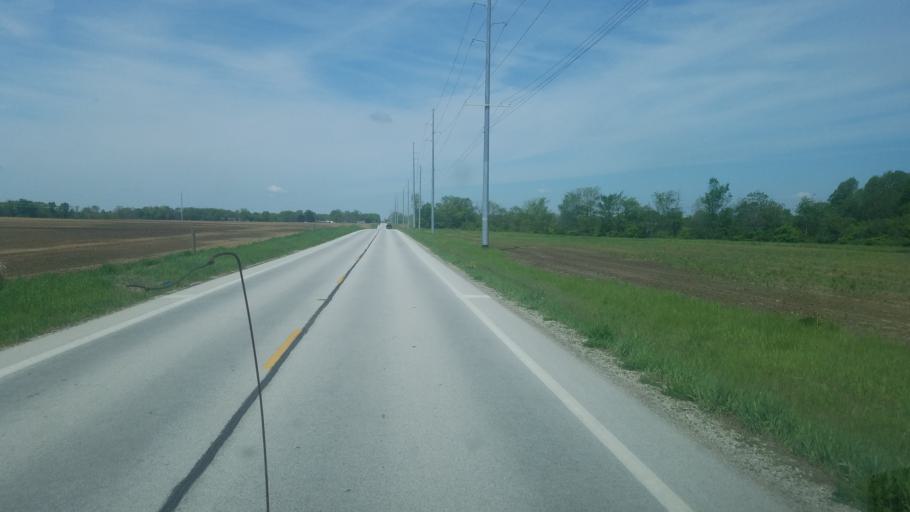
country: US
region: Ohio
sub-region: Seneca County
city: Tiffin
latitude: 41.0807
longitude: -83.1191
